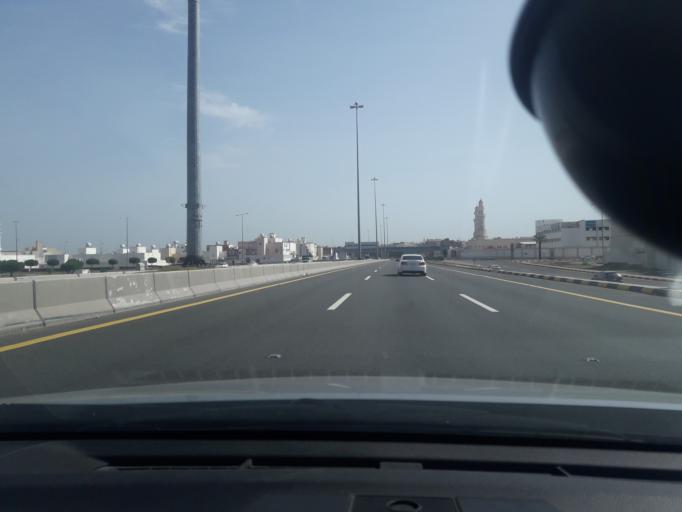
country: SA
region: Al Madinah al Munawwarah
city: Medina
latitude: 24.4446
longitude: 39.6450
